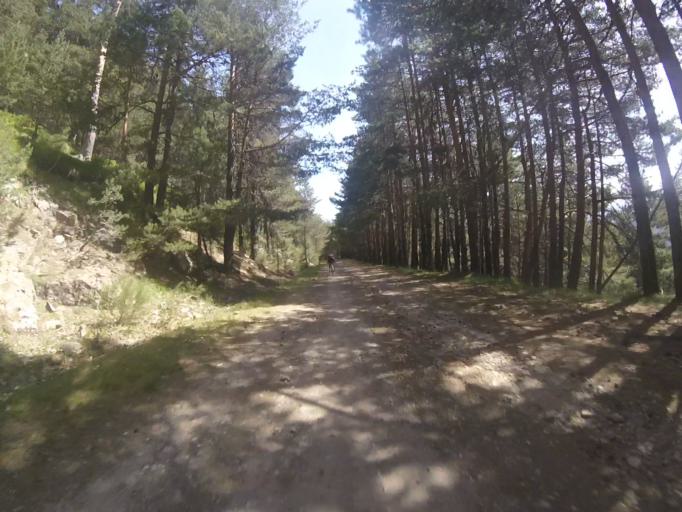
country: ES
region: Madrid
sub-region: Provincia de Madrid
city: Cercedilla
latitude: 40.8007
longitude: -4.0594
